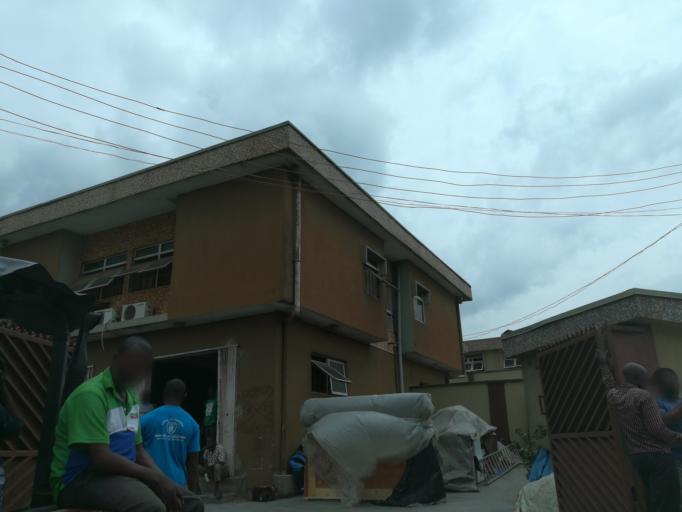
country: NG
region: Lagos
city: Oshodi
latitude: 6.5557
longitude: 3.3258
